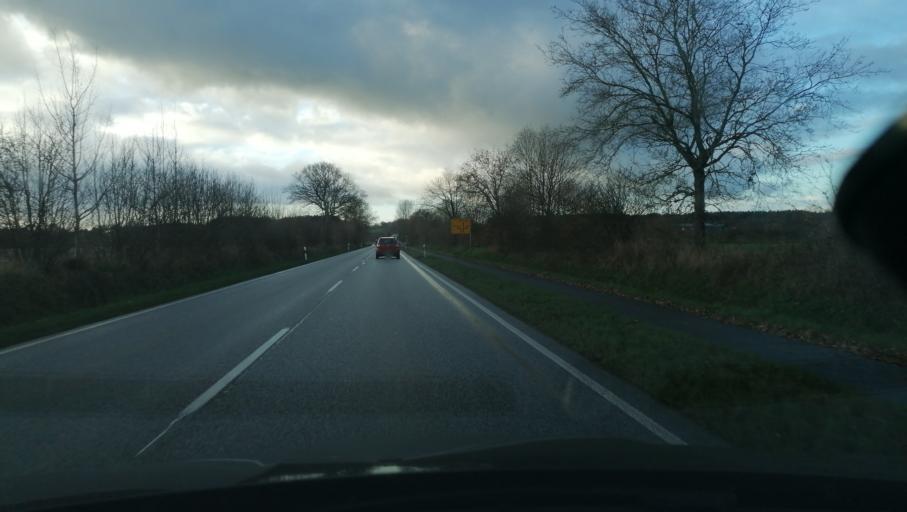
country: DE
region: Schleswig-Holstein
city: Tensbuttel-Rost
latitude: 54.1142
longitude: 9.2488
